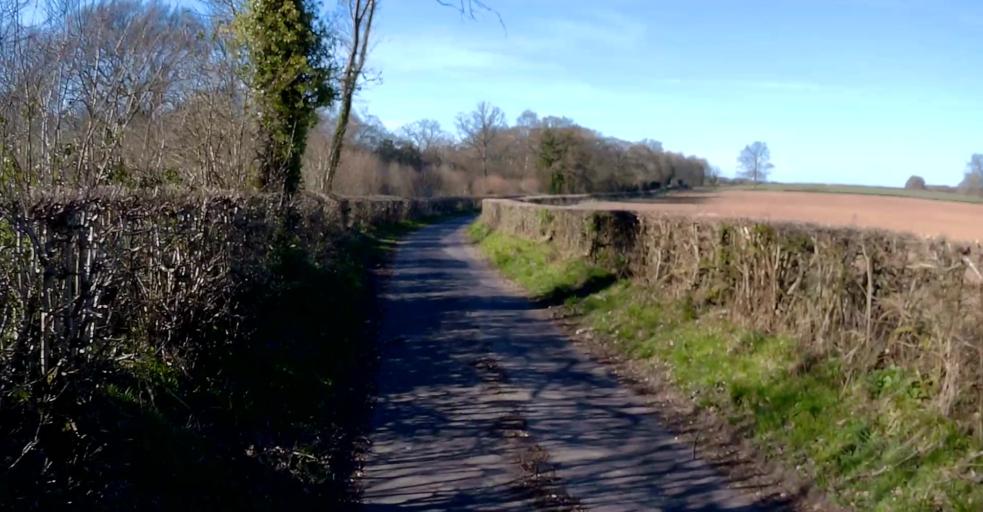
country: GB
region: England
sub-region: Hampshire
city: Old Basing
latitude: 51.2361
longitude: -1.0380
